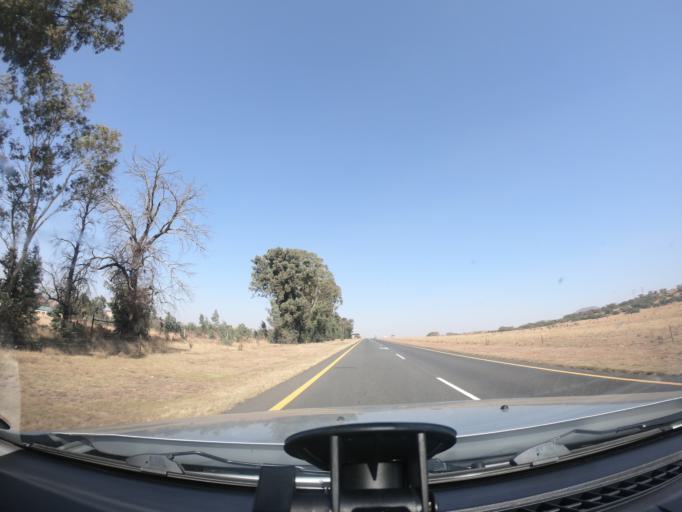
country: ZA
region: KwaZulu-Natal
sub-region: uThukela District Municipality
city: Ekuvukeni
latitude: -28.3657
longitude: 29.9540
